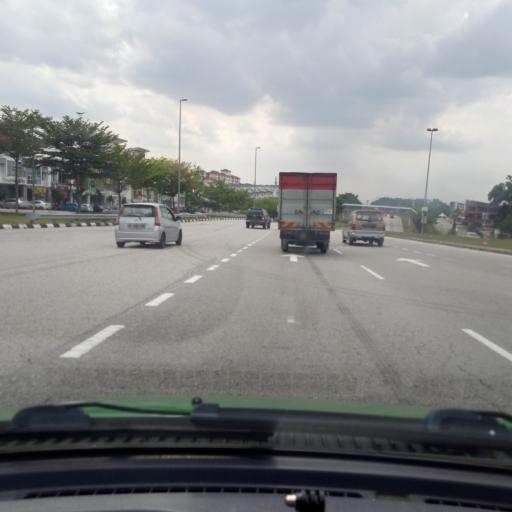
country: MY
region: Selangor
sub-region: Hulu Langat
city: Semenyih
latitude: 2.9905
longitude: 101.8199
